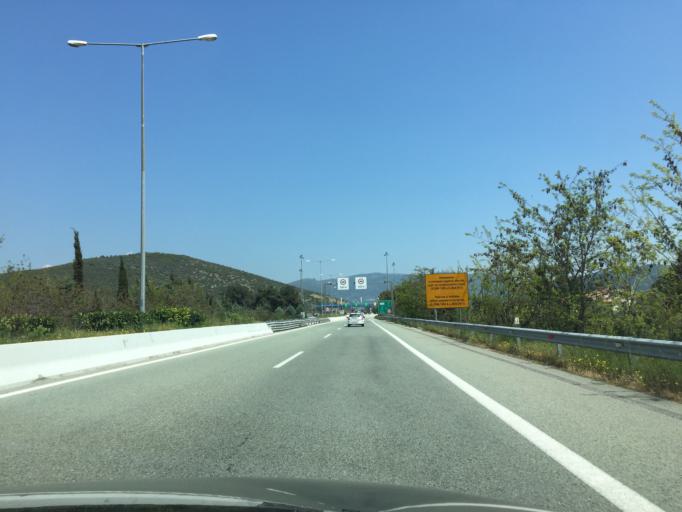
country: GR
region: Central Greece
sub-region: Nomos Fthiotidos
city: Pelasgia
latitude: 38.9177
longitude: 22.8429
